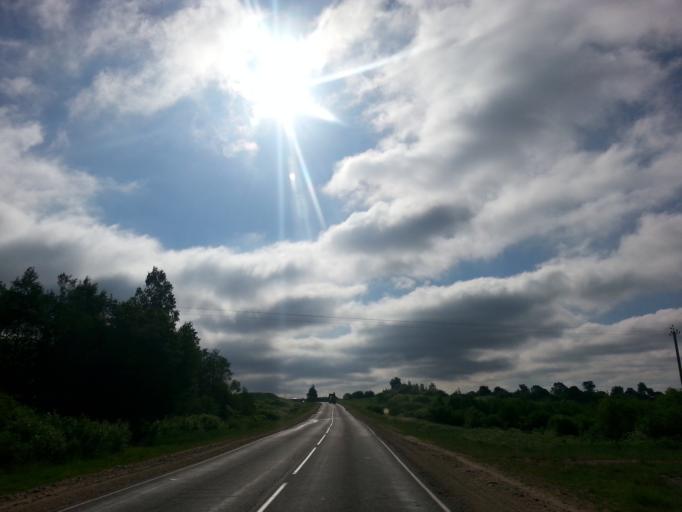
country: BY
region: Vitebsk
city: Mosar
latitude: 55.0616
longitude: 27.2243
